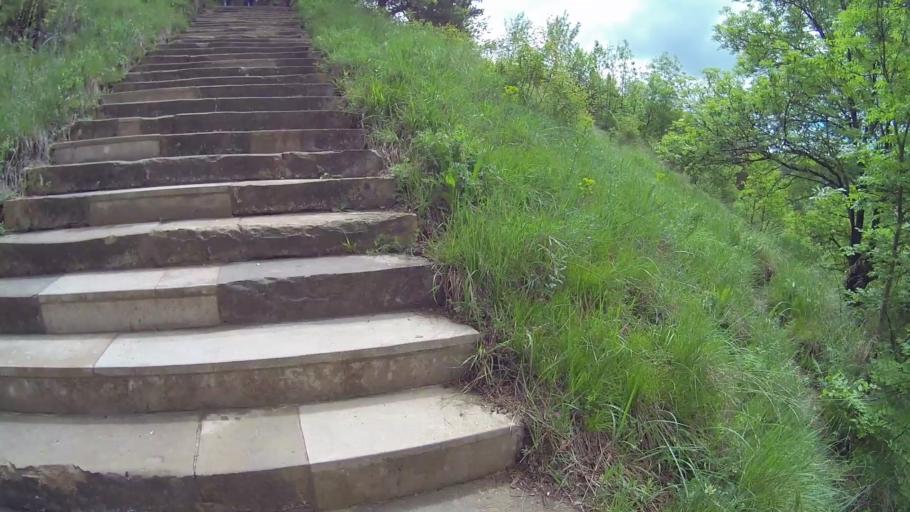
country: RU
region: Stavropol'skiy
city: Kislovodsk
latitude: 43.8927
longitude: 42.7221
